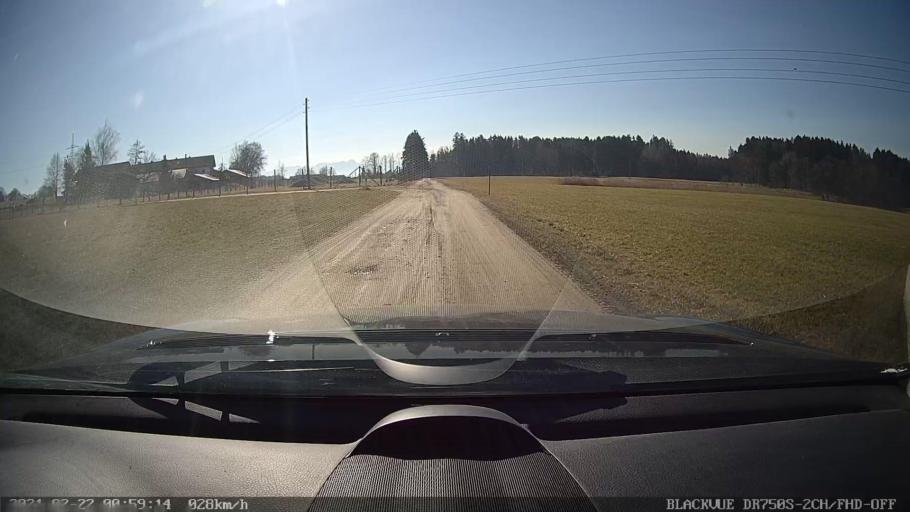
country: DE
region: Bavaria
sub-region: Upper Bavaria
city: Griesstatt
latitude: 47.9758
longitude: 12.1743
